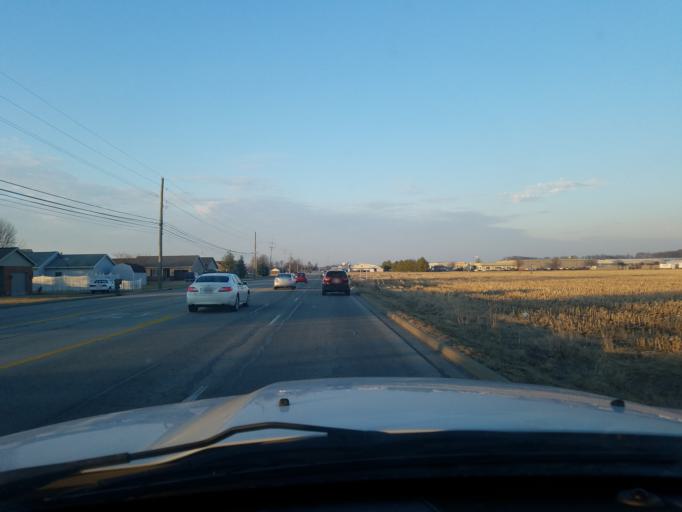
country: US
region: Indiana
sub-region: Vanderburgh County
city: Melody Hill
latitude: 38.0037
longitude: -87.4739
